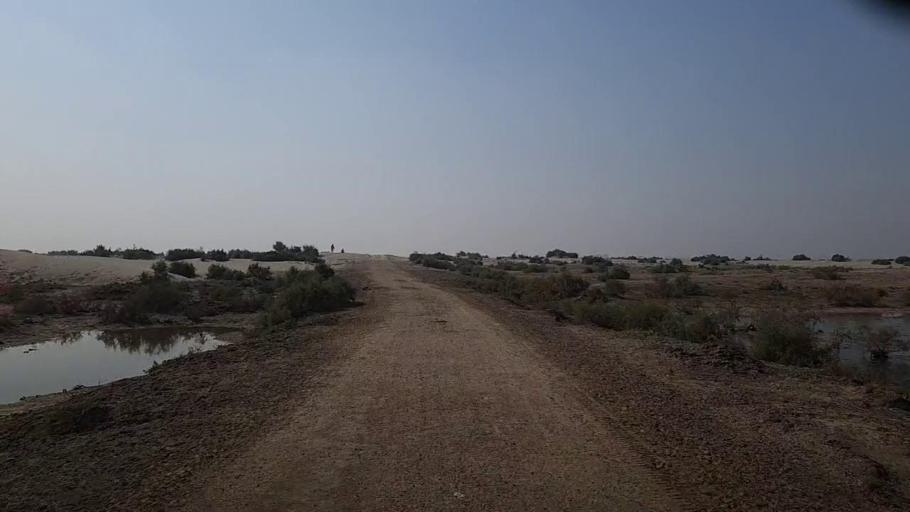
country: PK
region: Sindh
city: Bozdar
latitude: 27.2276
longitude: 68.5901
